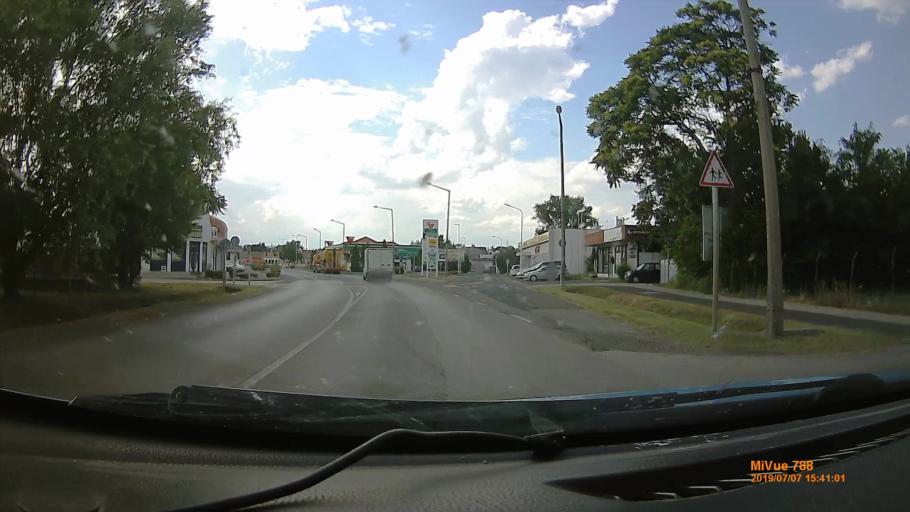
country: HU
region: Jasz-Nagykun-Szolnok
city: Jaszbereny
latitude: 47.5005
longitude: 19.9244
